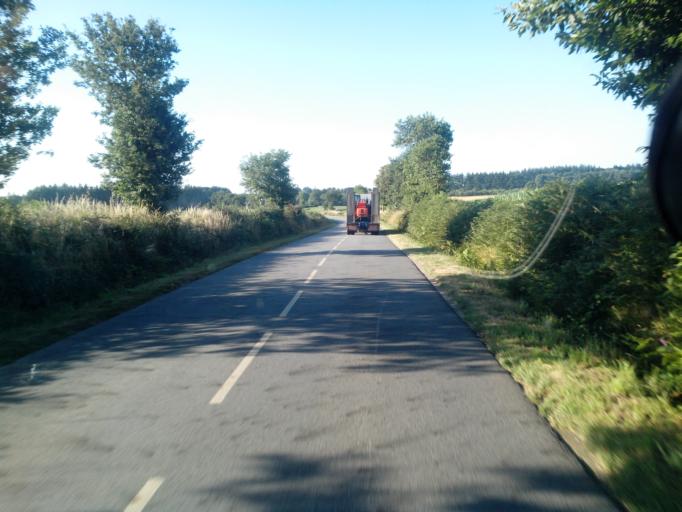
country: FR
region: Brittany
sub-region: Departement du Morbihan
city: Guilliers
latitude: 48.0520
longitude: -2.4117
